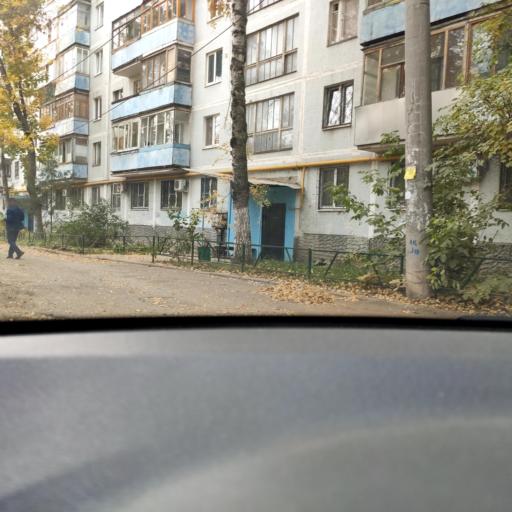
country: RU
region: Samara
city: Samara
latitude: 53.2468
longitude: 50.2320
